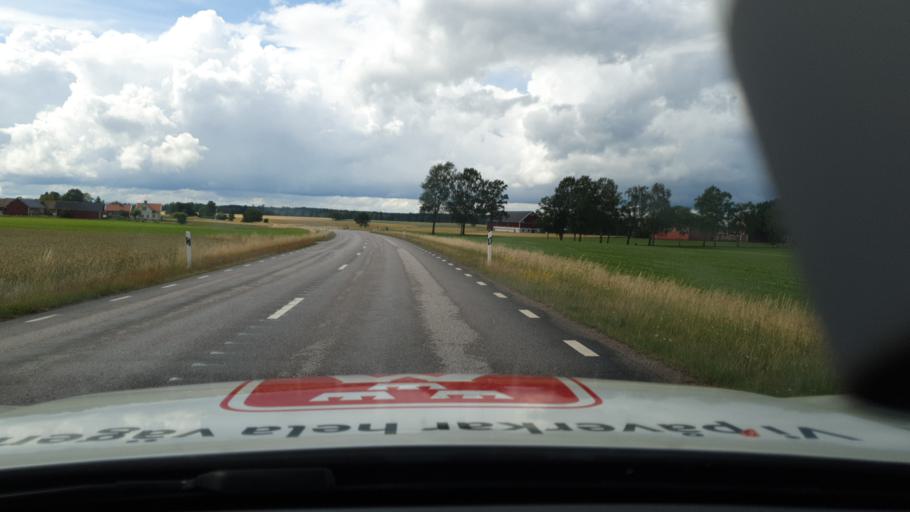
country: SE
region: Vaestra Goetaland
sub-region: Tibro Kommun
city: Tibro
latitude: 58.3461
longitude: 14.1464
